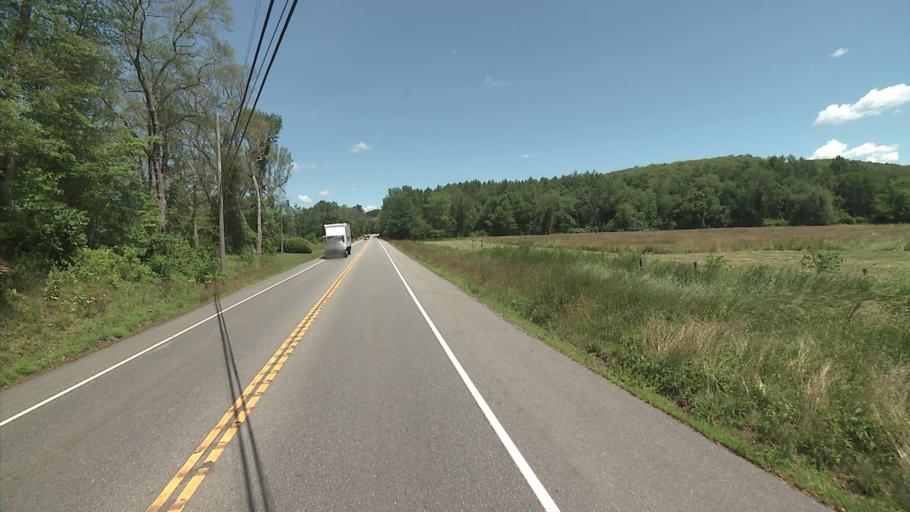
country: US
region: Connecticut
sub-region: New London County
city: Old Mystic
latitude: 41.4594
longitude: -71.9084
